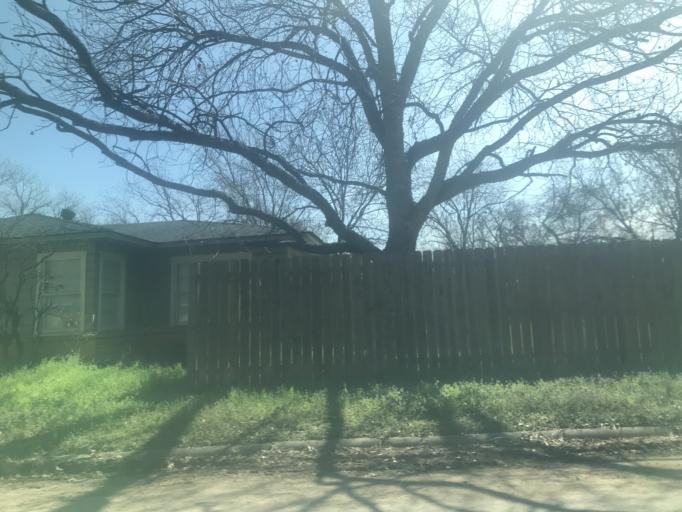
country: US
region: Texas
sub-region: Taylor County
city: Abilene
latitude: 32.4395
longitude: -99.7758
